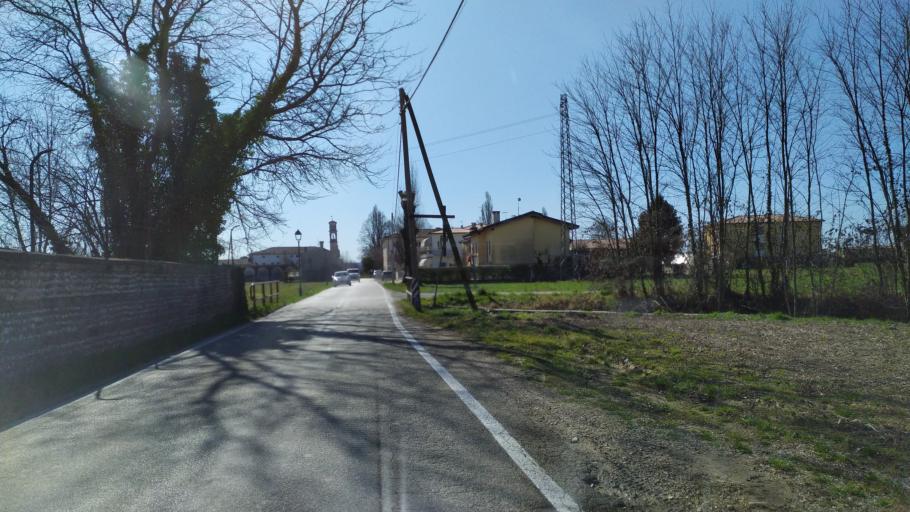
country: IT
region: Veneto
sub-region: Provincia di Vicenza
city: Vigardolo
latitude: 45.6295
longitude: 11.6013
